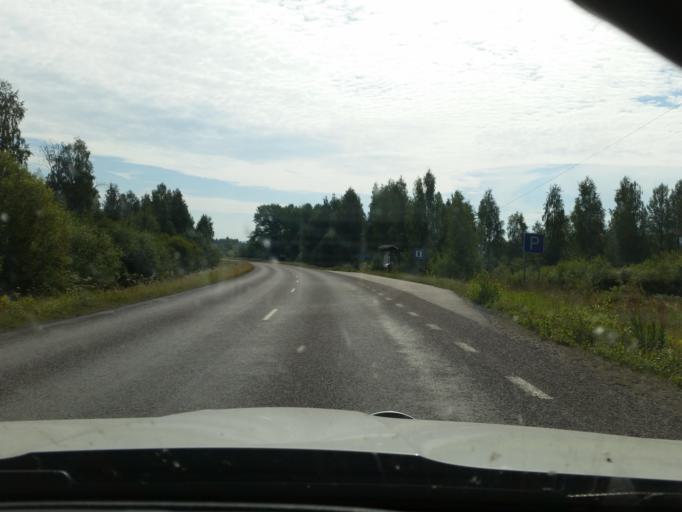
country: SE
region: Norrbotten
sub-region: Alvsbyns Kommun
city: AElvsbyn
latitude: 65.6943
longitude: 20.5938
